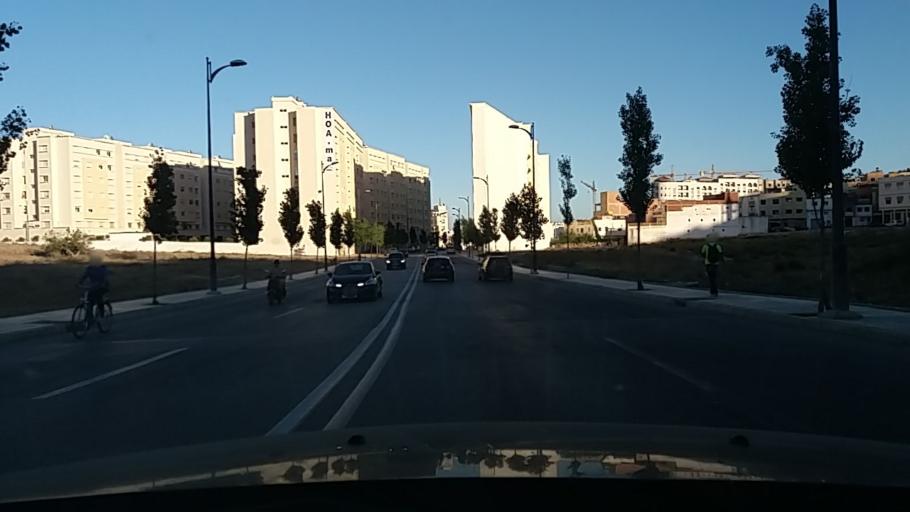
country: MA
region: Tanger-Tetouan
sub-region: Tanger-Assilah
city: Boukhalef
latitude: 35.7677
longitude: -5.8589
